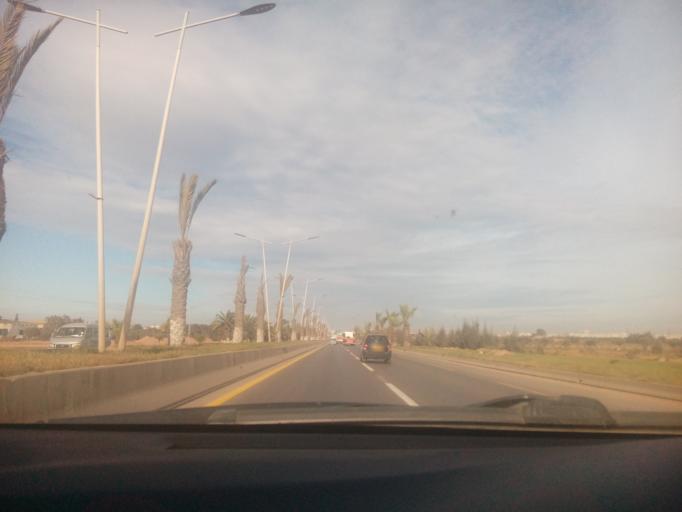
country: DZ
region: Oran
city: Es Senia
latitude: 35.6583
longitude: -0.5926
